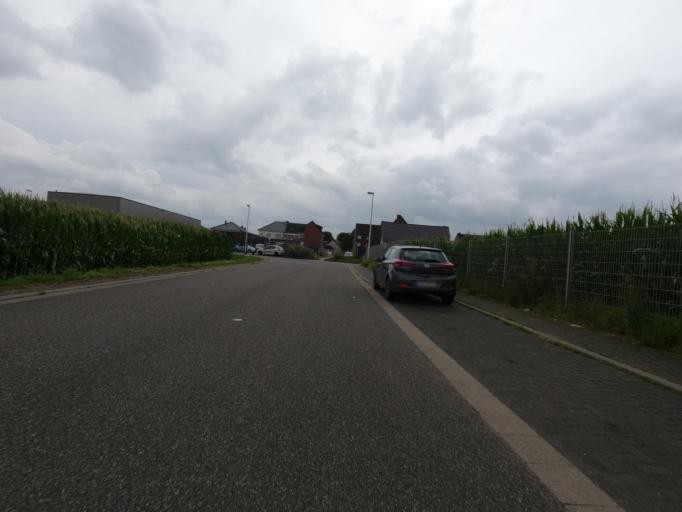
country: DE
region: North Rhine-Westphalia
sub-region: Regierungsbezirk Koln
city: Ubach-Palenberg
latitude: 50.9136
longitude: 6.1444
